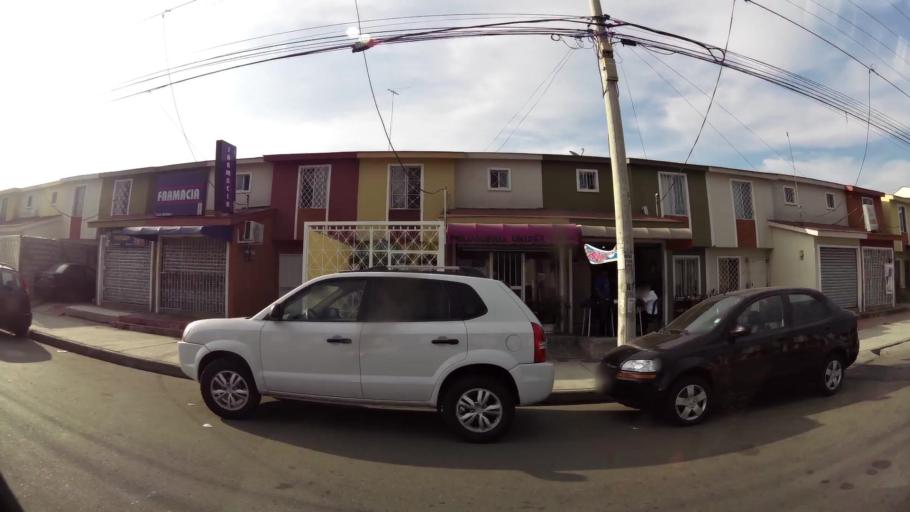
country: EC
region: Guayas
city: Eloy Alfaro
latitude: -2.0680
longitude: -79.8983
